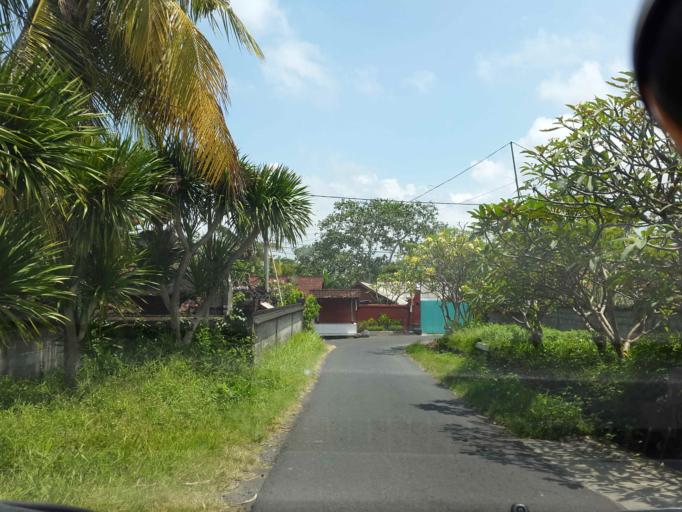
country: ID
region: Bali
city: Klungkung
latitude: -8.5554
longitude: 115.3850
